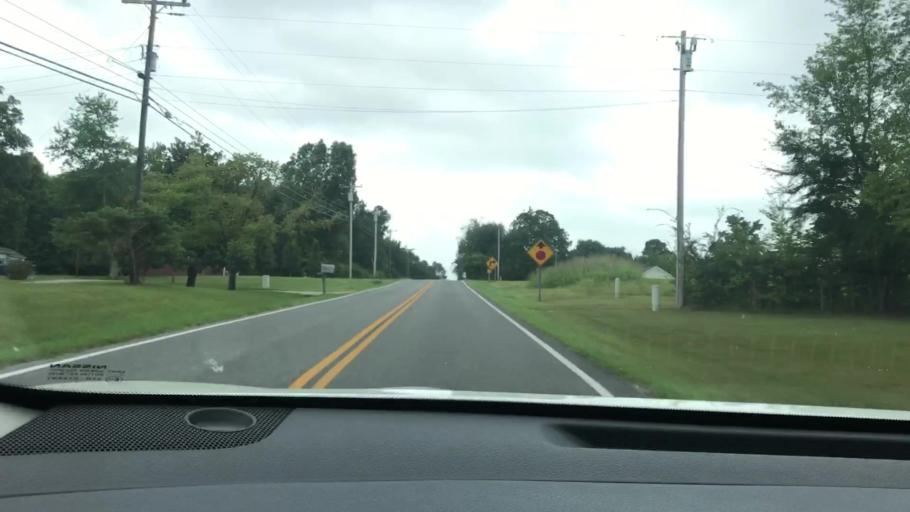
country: US
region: Kentucky
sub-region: Calloway County
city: Murray
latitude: 36.6798
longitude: -88.3007
